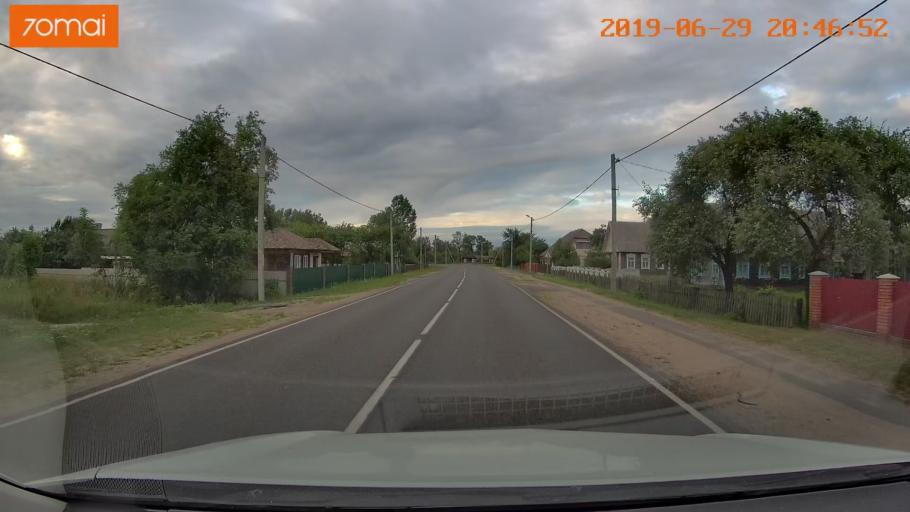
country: BY
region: Brest
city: Hantsavichy
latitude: 52.6335
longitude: 26.3121
